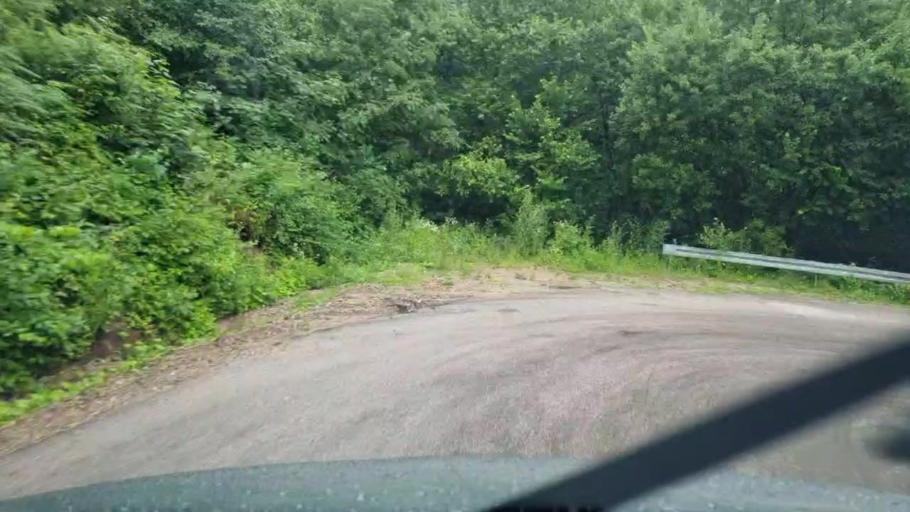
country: BA
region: Federation of Bosnia and Herzegovina
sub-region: Bosansko-Podrinjski Kanton
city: Ustikolina
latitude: 43.6346
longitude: 18.6256
